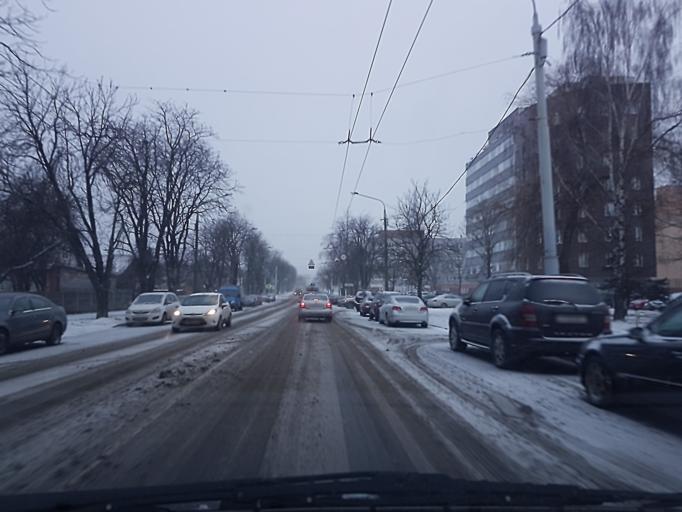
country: BY
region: Minsk
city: Minsk
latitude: 53.9019
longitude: 27.5150
